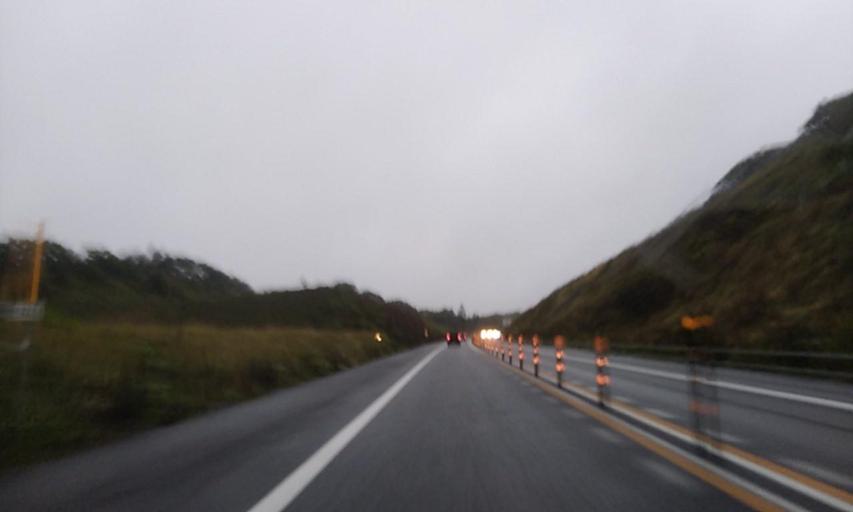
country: JP
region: Hokkaido
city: Kushiro
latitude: 43.0027
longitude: 144.4970
